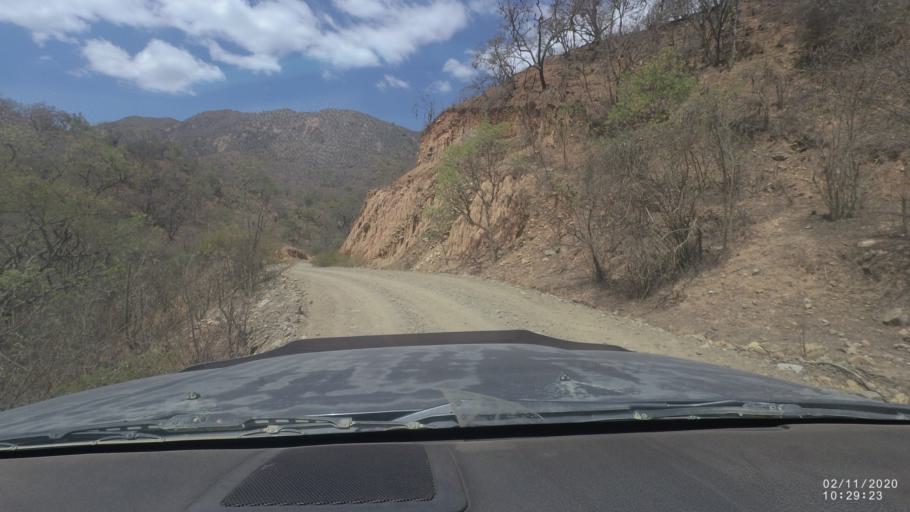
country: BO
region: Cochabamba
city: Aiquile
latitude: -18.3410
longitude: -64.7648
